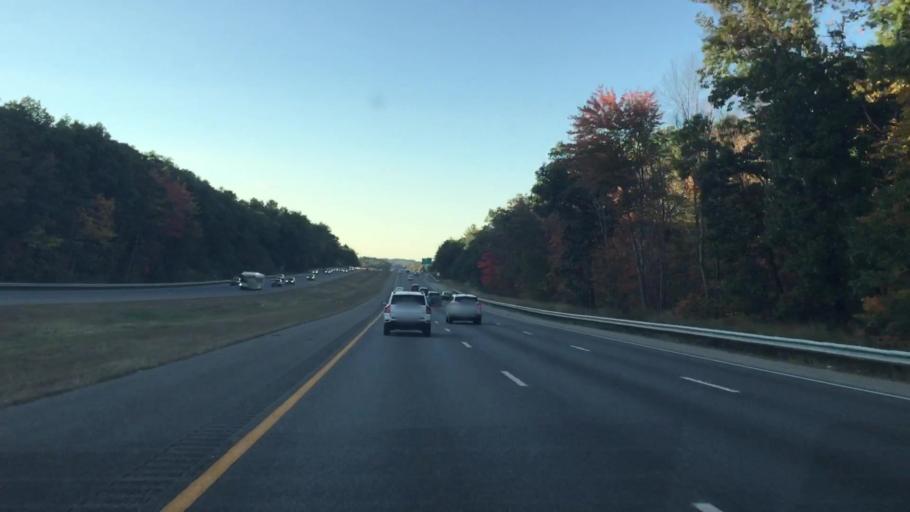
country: US
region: Massachusetts
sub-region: Middlesex County
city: Pinehurst
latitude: 42.4946
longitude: -71.2355
